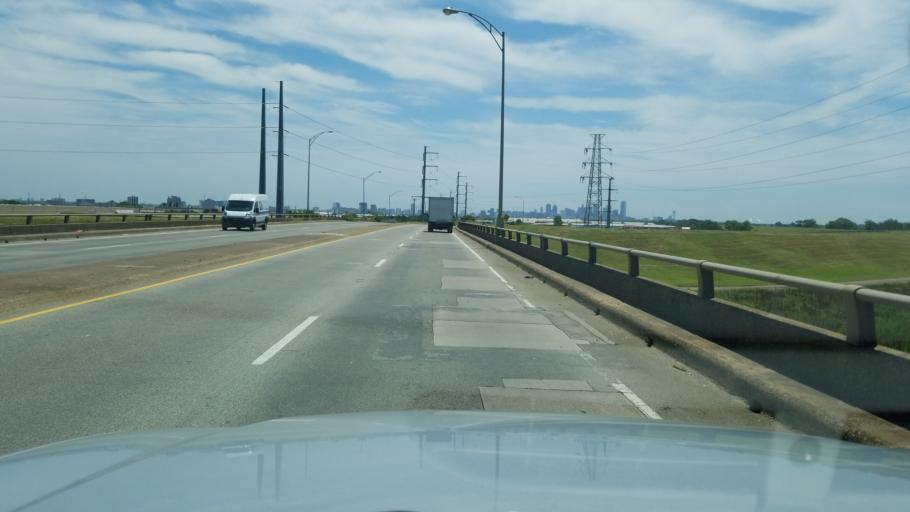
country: US
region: Texas
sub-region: Dallas County
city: Irving
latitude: 32.8087
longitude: -96.9051
